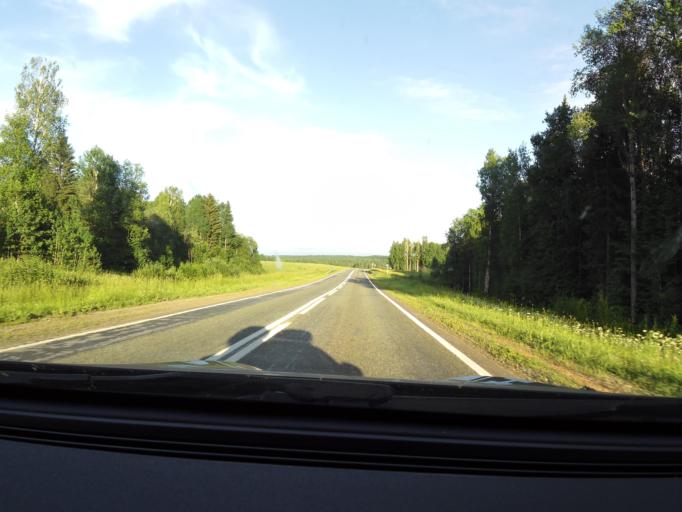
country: RU
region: Perm
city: Siva
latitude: 58.6375
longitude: 53.8492
